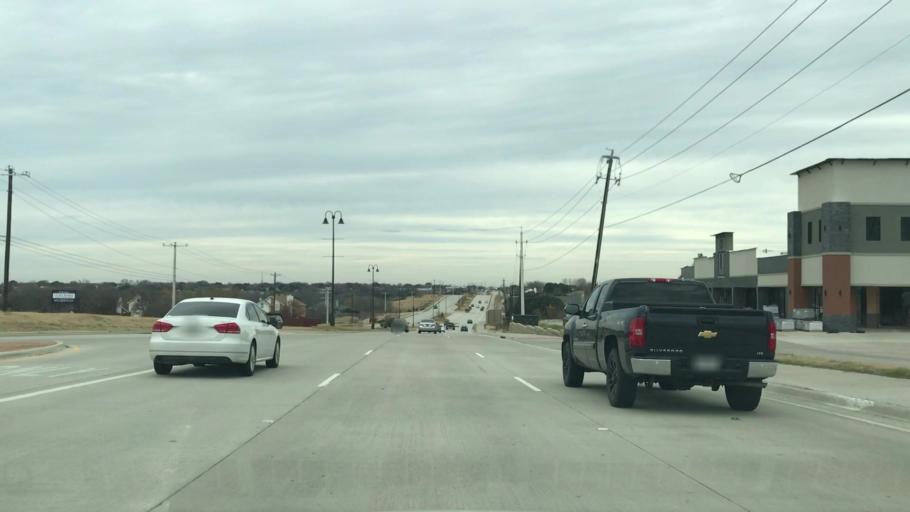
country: US
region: Texas
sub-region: Denton County
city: The Colony
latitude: 33.0822
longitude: -96.8927
